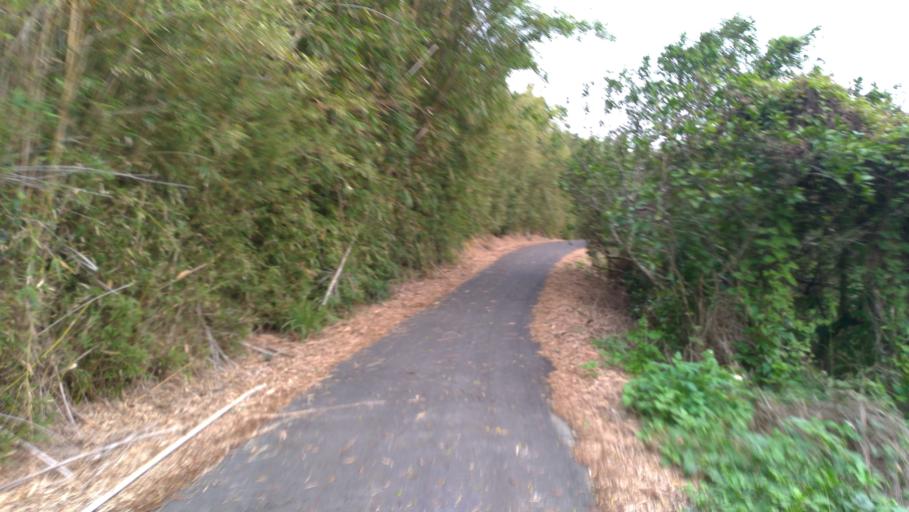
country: TW
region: Taiwan
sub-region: Hsinchu
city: Hsinchu
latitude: 24.7551
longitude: 120.9785
